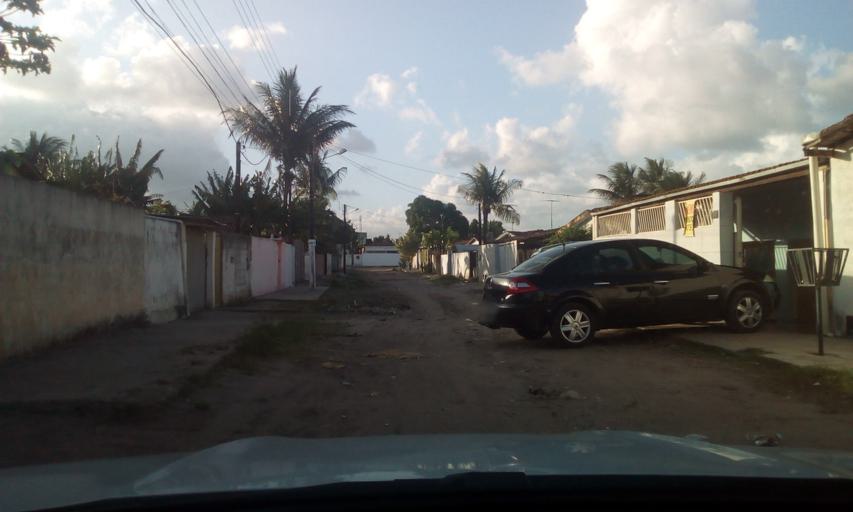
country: BR
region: Paraiba
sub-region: Conde
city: Conde
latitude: -7.2026
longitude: -34.8597
